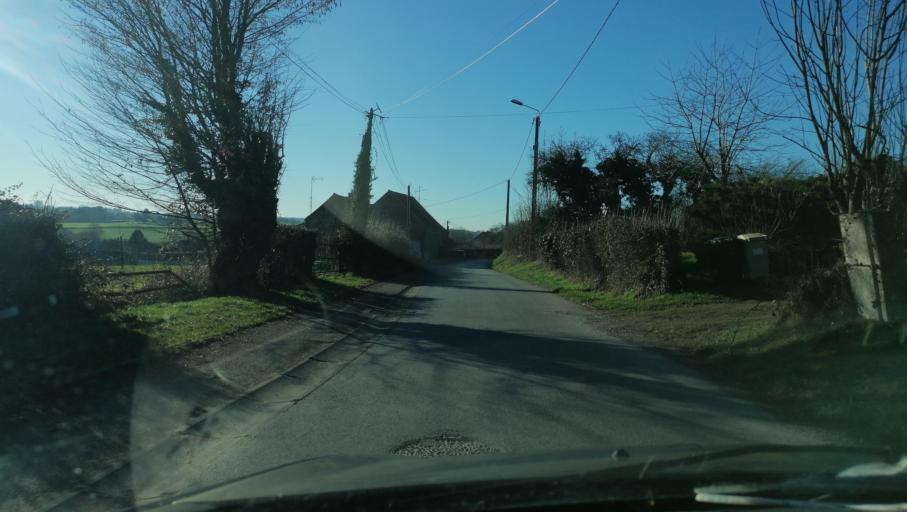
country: FR
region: Nord-Pas-de-Calais
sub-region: Departement du Nord
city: Ferriere-la-Grande
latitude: 50.2209
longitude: 4.0293
